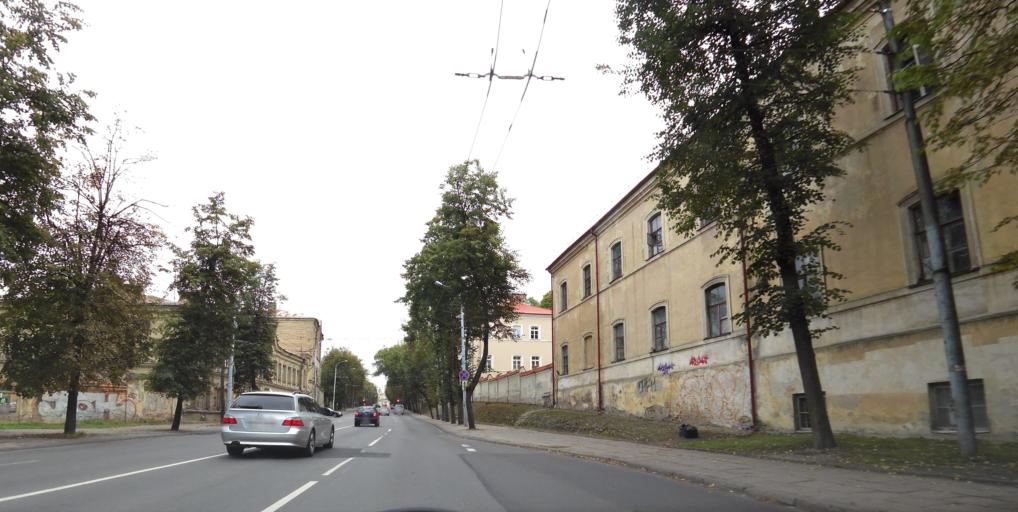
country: LT
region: Vilnius County
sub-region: Vilnius
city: Vilnius
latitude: 54.6896
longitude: 25.2956
